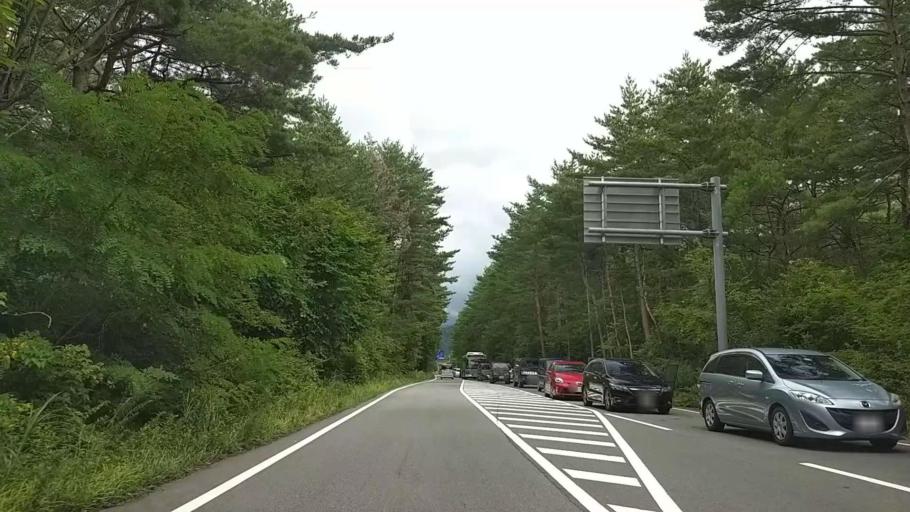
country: JP
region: Yamanashi
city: Fujikawaguchiko
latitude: 35.4824
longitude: 138.7694
